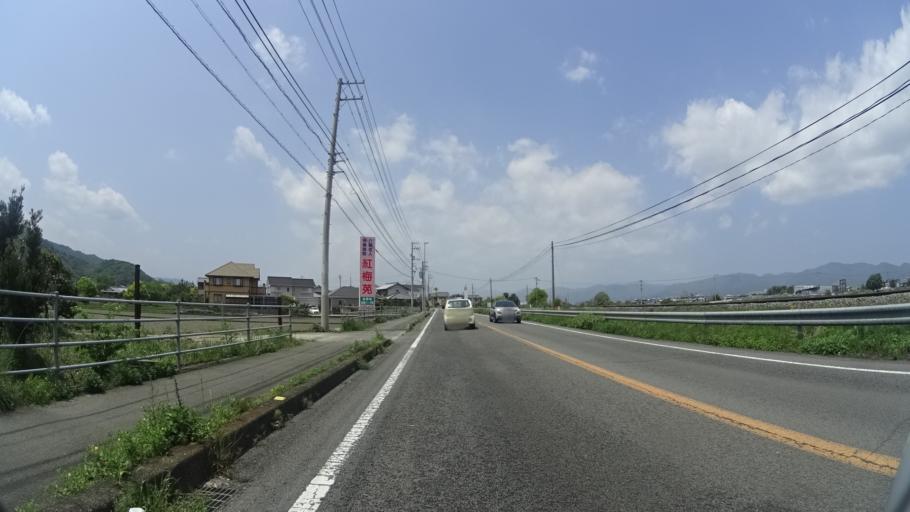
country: JP
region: Tokushima
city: Ishii
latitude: 34.0668
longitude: 134.4264
